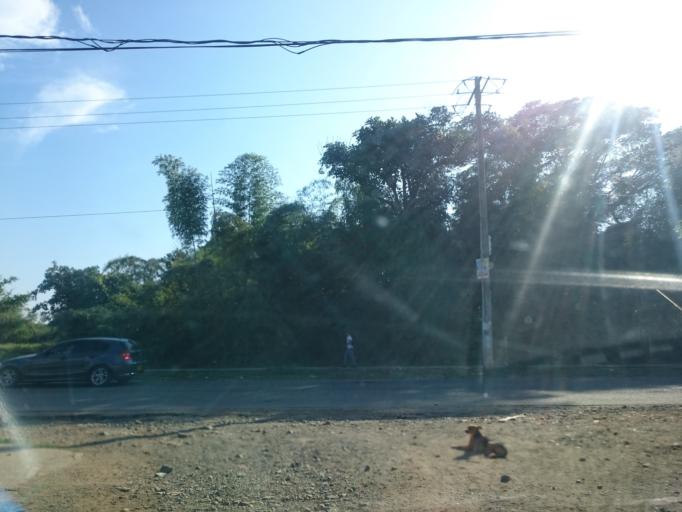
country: CO
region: Cauca
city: Santander de Quilichao
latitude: 3.0162
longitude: -76.4918
